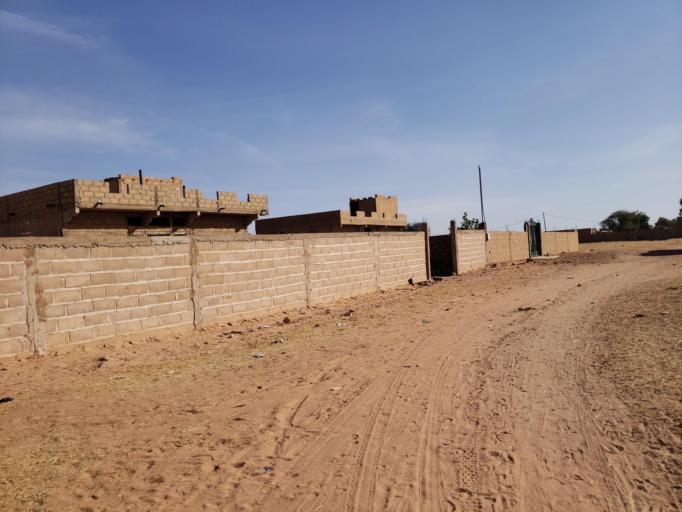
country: SN
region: Matam
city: Ranerou
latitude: 15.3024
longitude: -13.9599
